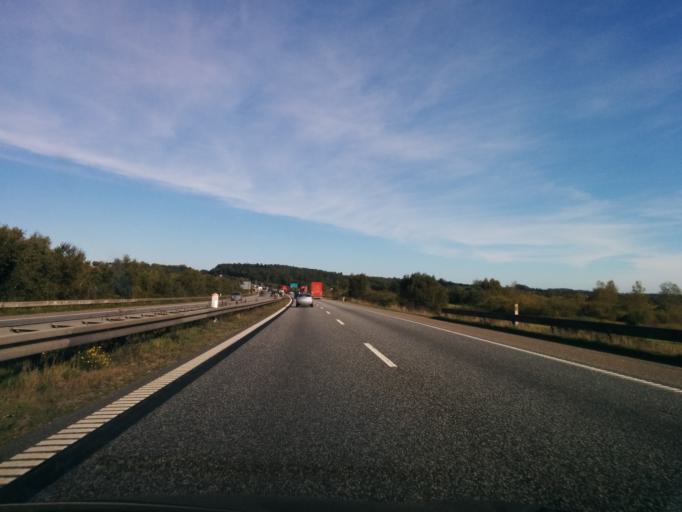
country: DK
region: Central Jutland
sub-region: Horsens Kommune
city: Horsens
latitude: 55.8896
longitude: 9.7998
